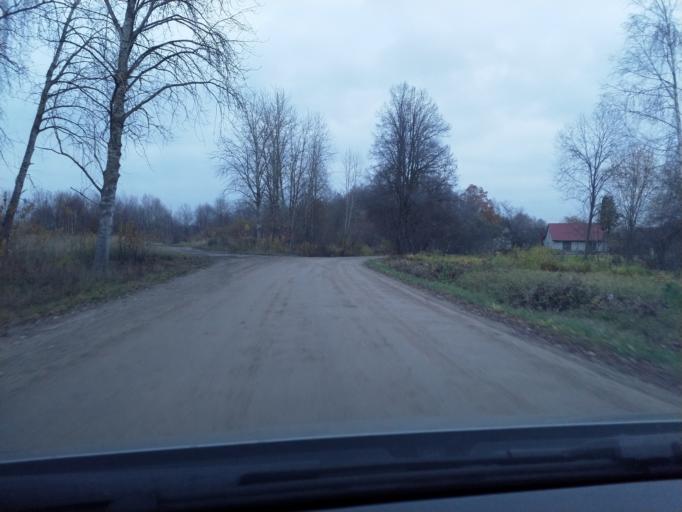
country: LV
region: Kuldigas Rajons
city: Kuldiga
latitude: 56.9643
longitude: 21.9831
